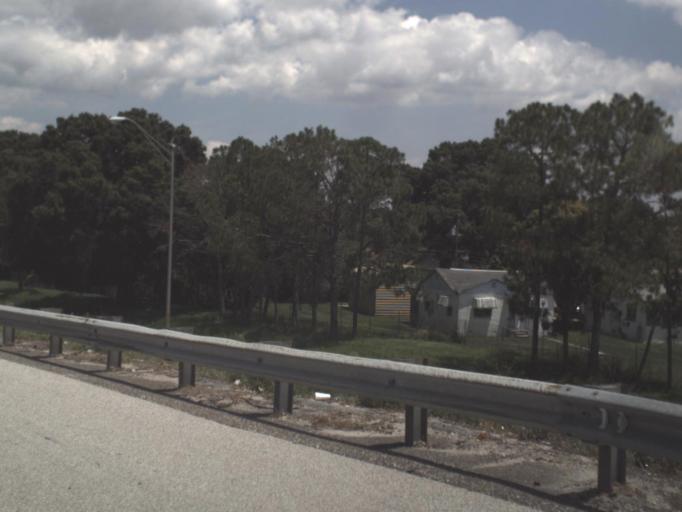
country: US
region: Florida
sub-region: Pinellas County
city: Lealman
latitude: 27.8080
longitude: -82.6626
